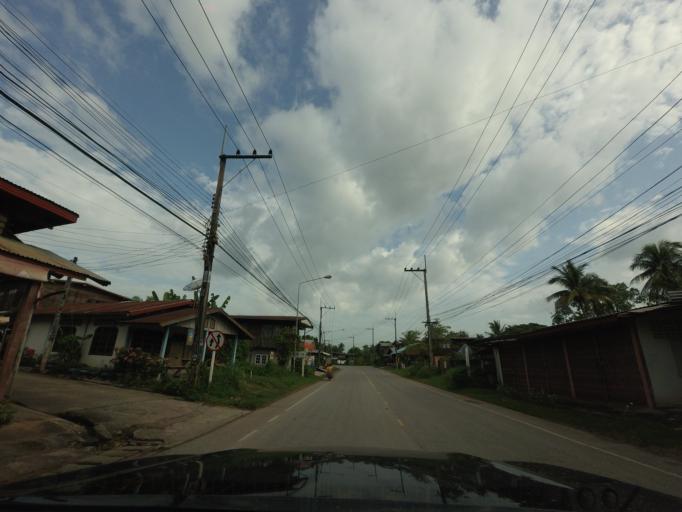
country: TH
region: Nong Khai
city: Pho Tak
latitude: 17.7782
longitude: 102.3949
